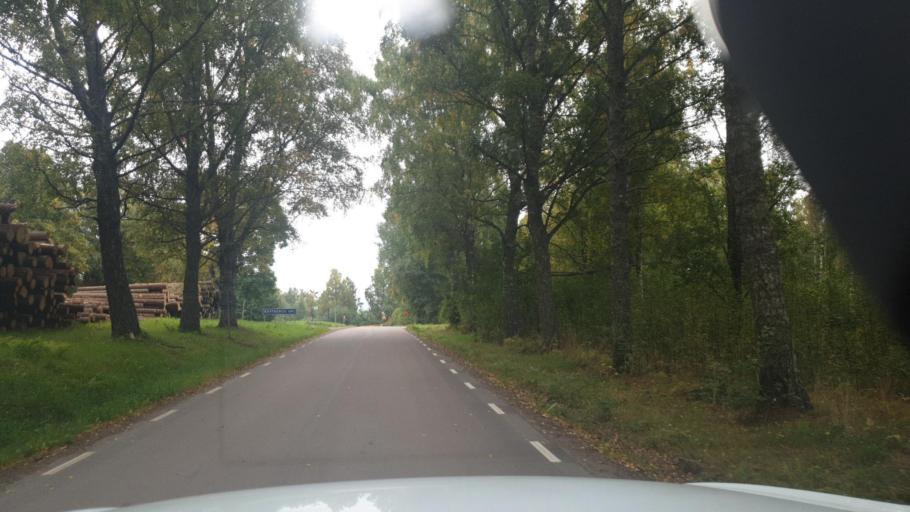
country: SE
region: Vaermland
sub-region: Sunne Kommun
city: Sunne
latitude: 59.7957
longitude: 13.1265
